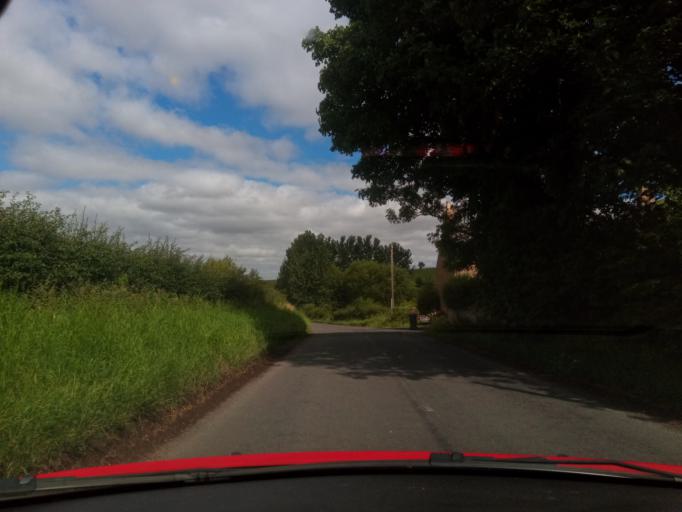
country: GB
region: Scotland
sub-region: The Scottish Borders
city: Kelso
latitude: 55.5361
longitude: -2.3634
